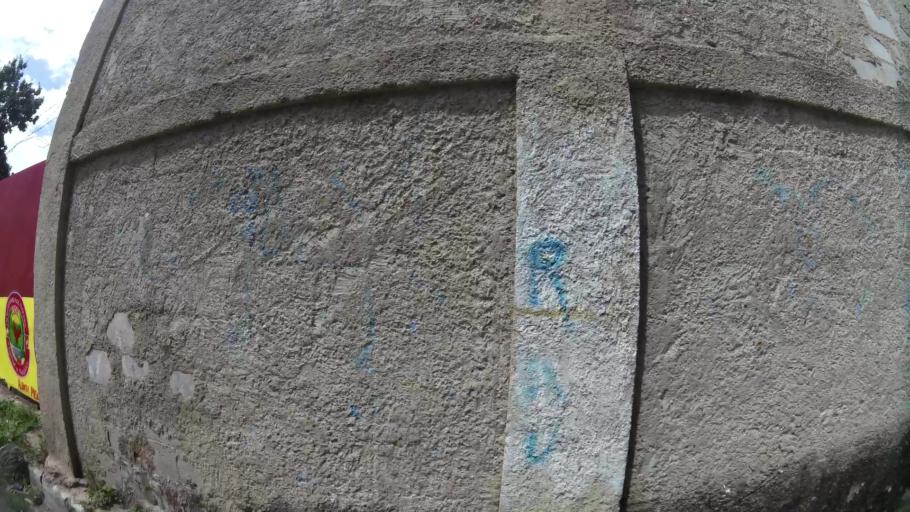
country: DO
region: San Cristobal
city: San Cristobal
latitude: 18.4168
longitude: -70.0976
